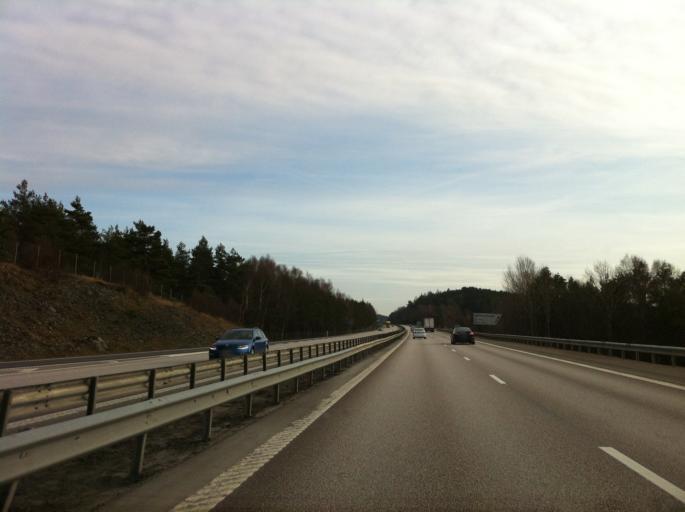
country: SE
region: Halland
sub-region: Kungsbacka Kommun
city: Kungsbacka
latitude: 57.4780
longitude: 12.0444
